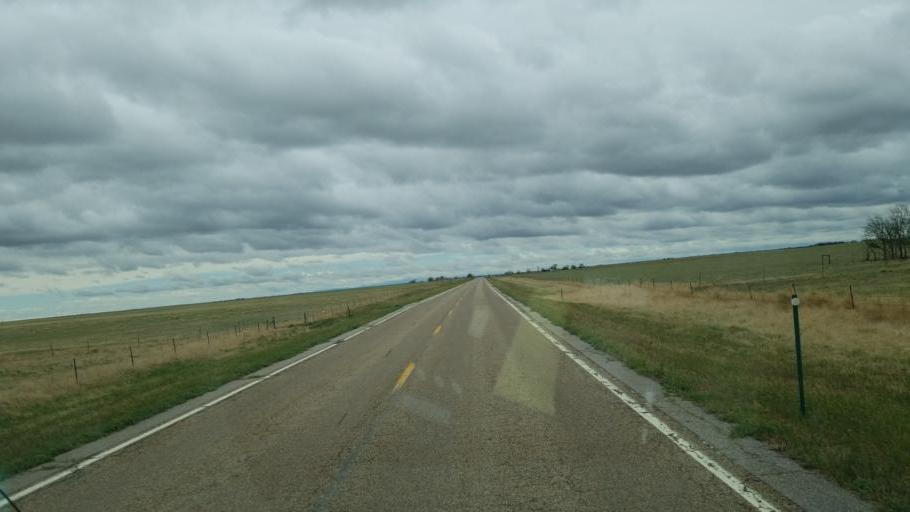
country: US
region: Colorado
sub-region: El Paso County
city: Ellicott
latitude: 38.8395
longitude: -103.9242
